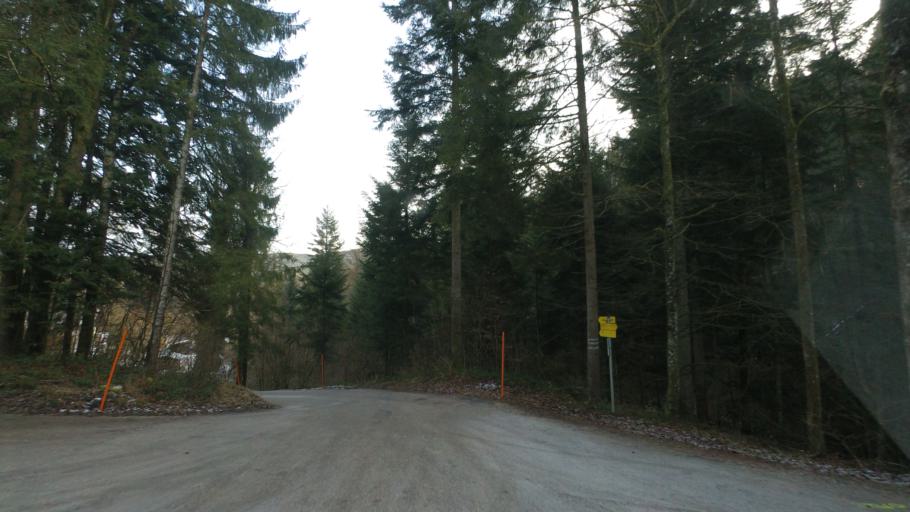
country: DE
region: Bavaria
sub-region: Upper Bavaria
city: Siegsdorf
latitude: 47.7934
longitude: 12.6347
